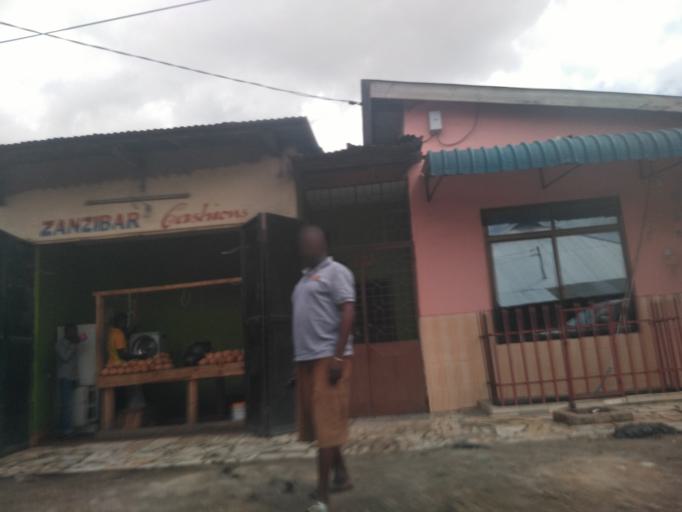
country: TZ
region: Dar es Salaam
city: Magomeni
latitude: -6.7882
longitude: 39.2480
